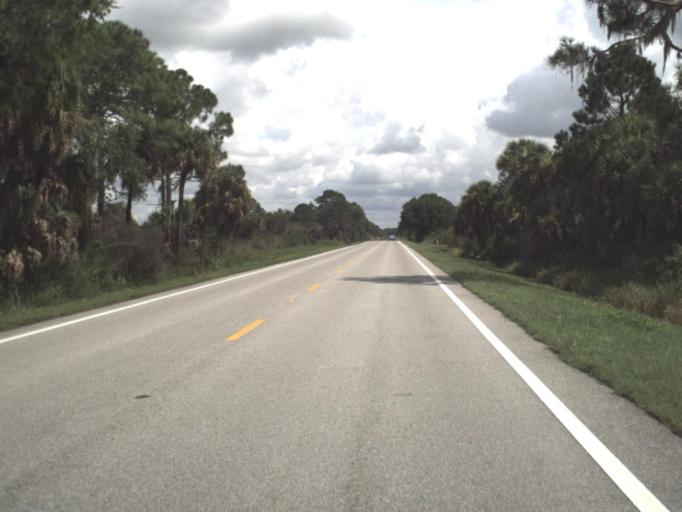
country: US
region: Florida
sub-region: Sarasota County
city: Warm Mineral Springs
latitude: 27.2024
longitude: -82.2384
